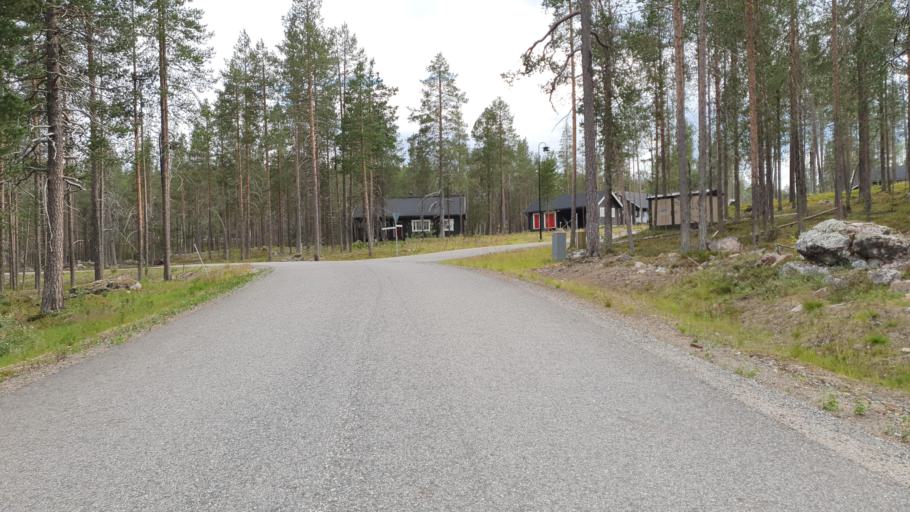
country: FI
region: Lapland
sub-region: Tunturi-Lappi
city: Kolari
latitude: 67.5907
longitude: 24.1243
